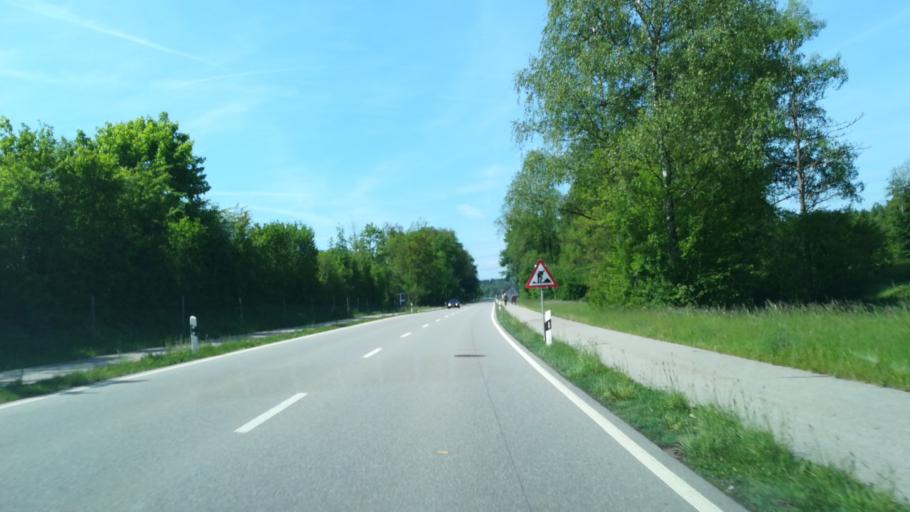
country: CH
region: Zurich
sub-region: Bezirk Pfaeffikon
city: Effretikon / Watt
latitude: 47.4435
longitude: 8.6928
